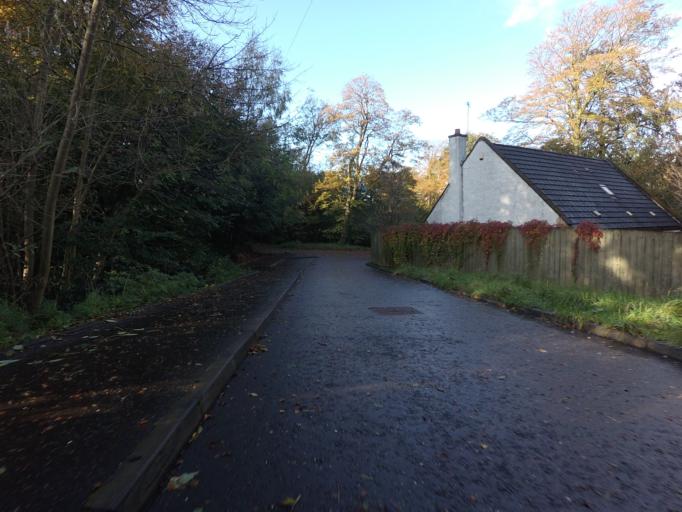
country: GB
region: Scotland
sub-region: West Lothian
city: West Calder
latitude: 55.8612
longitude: -3.5457
